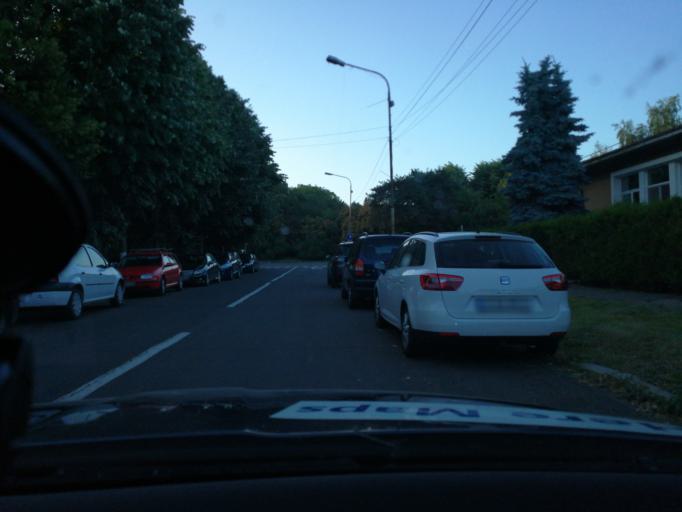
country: RO
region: Constanta
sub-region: Comuna Douazeci si Trei August
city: Douazeci si Trei August
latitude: 43.8744
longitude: 28.5999
